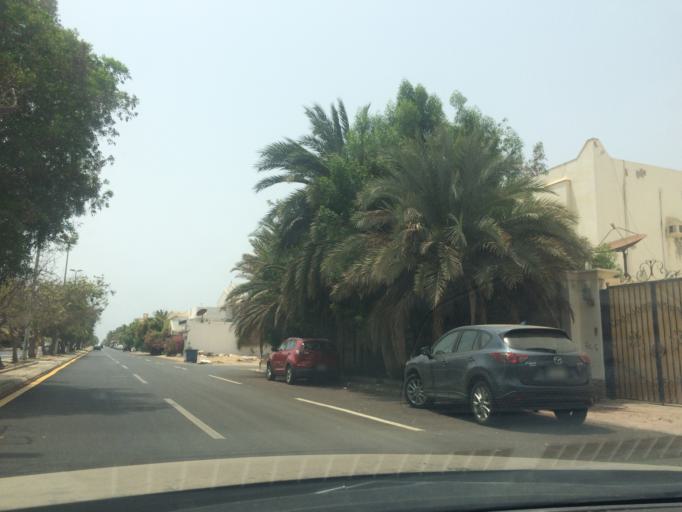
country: SA
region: Makkah
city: Jeddah
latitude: 21.5637
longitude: 39.1228
